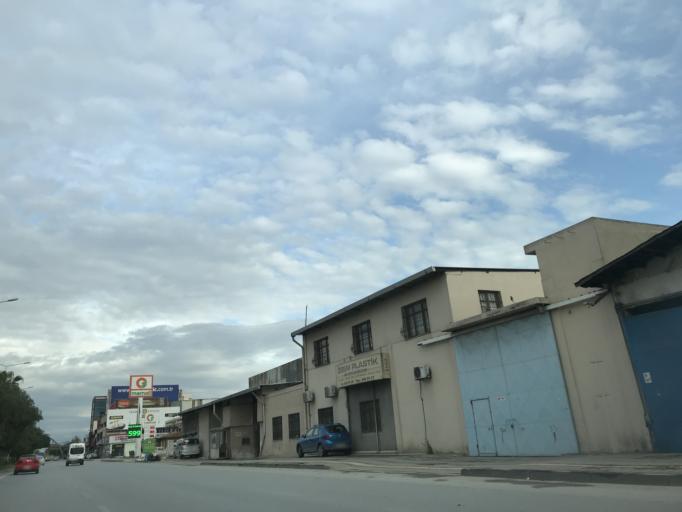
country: TR
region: Adana
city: Seyhan
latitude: 36.9945
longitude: 35.2833
